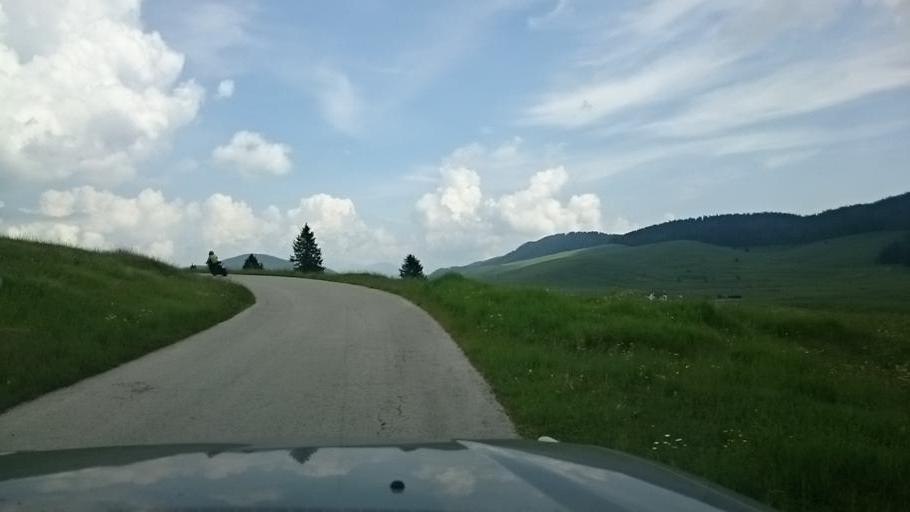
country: IT
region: Veneto
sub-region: Provincia di Vicenza
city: Foza
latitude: 45.9435
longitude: 11.6126
